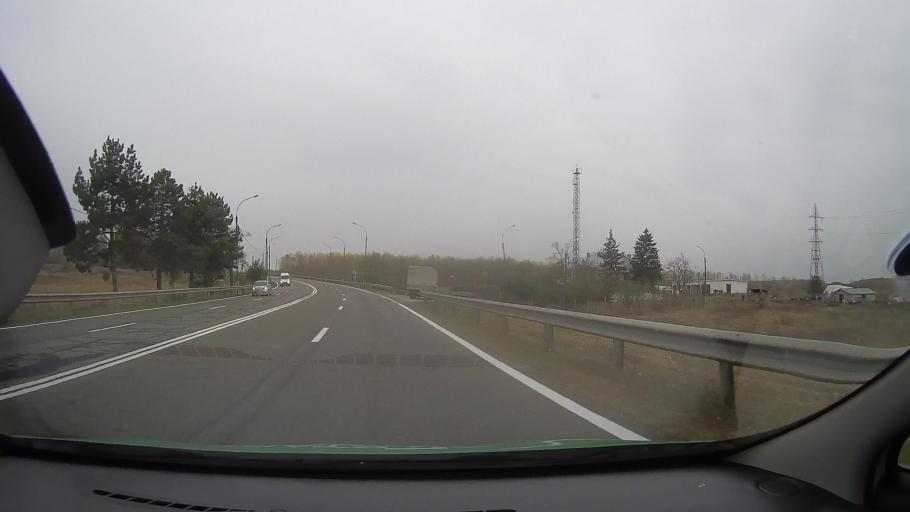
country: RO
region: Ialomita
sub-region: Comuna Giurgeni
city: Giurgeni
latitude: 44.7514
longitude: 27.8911
